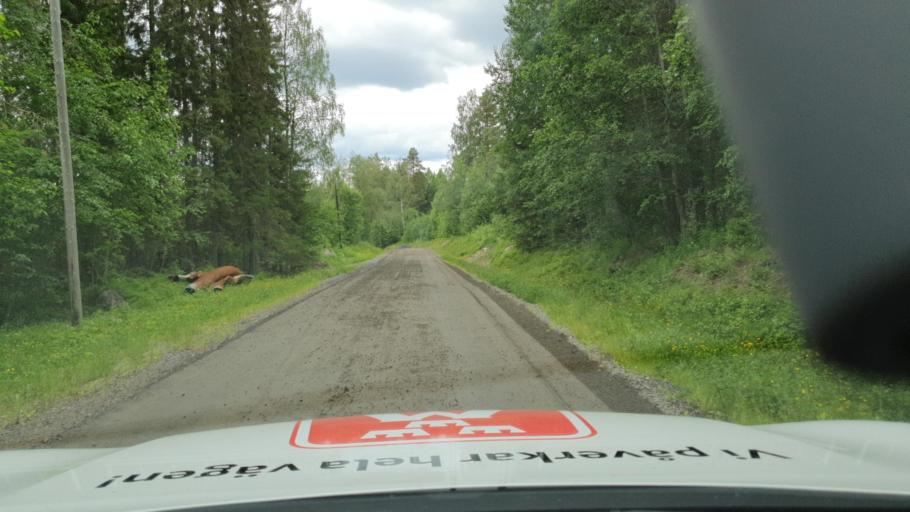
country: SE
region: Vaesterbotten
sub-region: Bjurholms Kommun
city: Bjurholm
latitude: 63.8134
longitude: 19.0371
